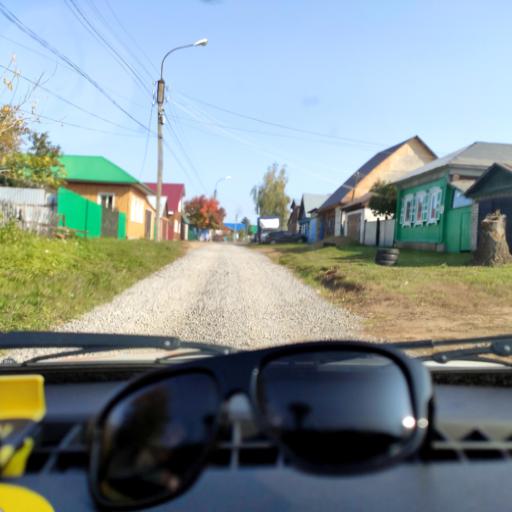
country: RU
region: Bashkortostan
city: Blagoveshchensk
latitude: 55.0250
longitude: 55.9939
